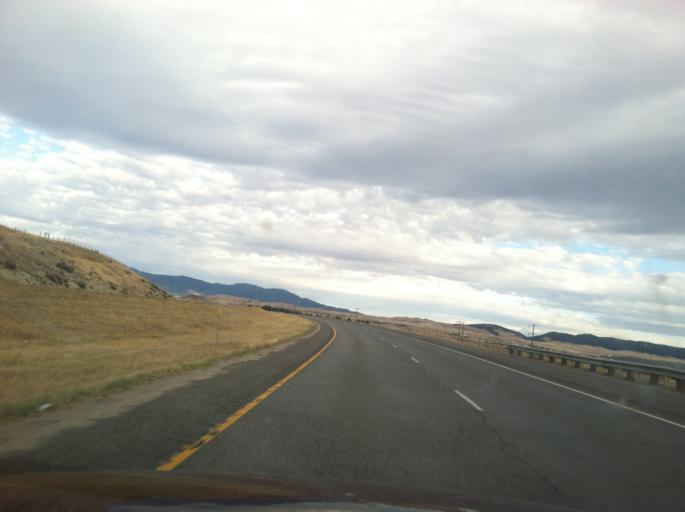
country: US
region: Montana
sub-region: Silver Bow County
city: Butte-Silver Bow (Balance)
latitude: 46.0108
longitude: -112.7096
